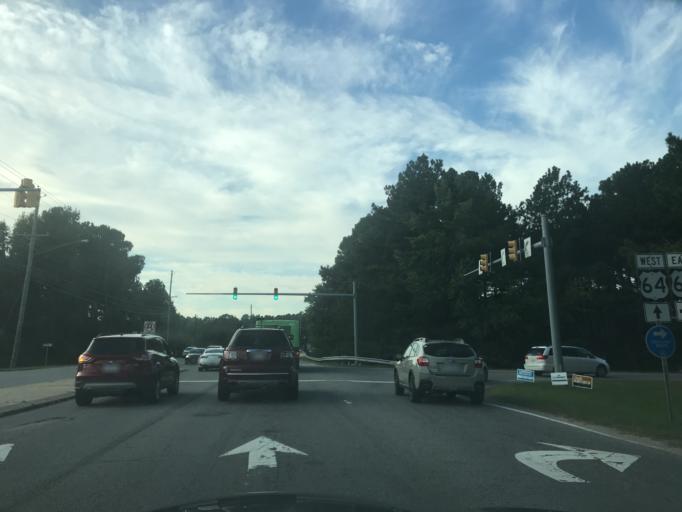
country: US
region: North Carolina
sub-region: Wake County
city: Apex
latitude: 35.7471
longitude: -78.8743
